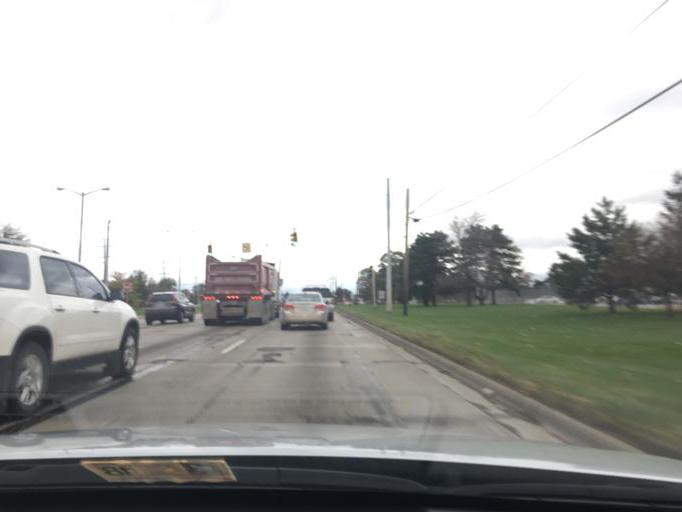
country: US
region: Michigan
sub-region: Macomb County
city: Sterling Heights
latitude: 42.5625
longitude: -83.0488
